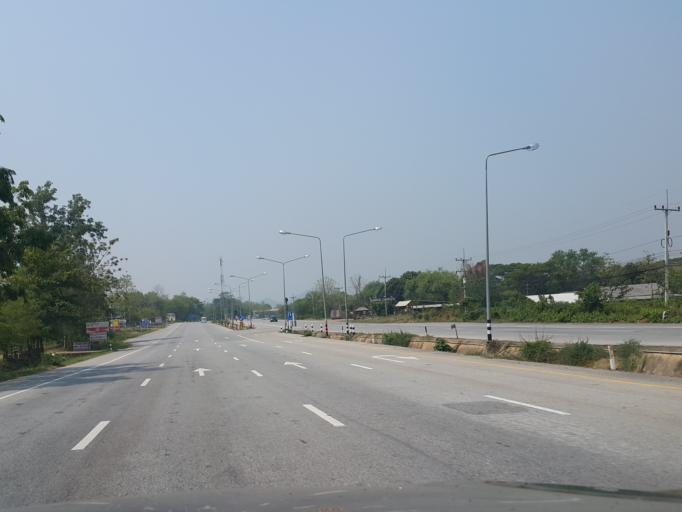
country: TH
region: Lampang
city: Thoen
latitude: 17.7372
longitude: 99.2336
